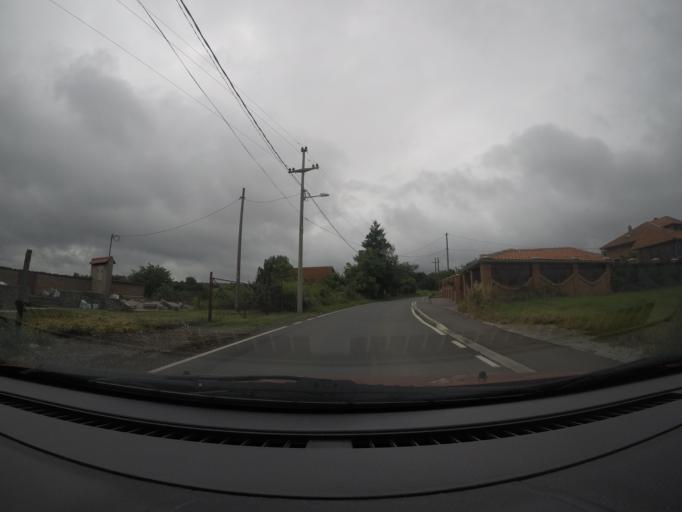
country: RS
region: Central Serbia
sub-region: Belgrade
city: Zvezdara
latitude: 44.7003
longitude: 20.5612
